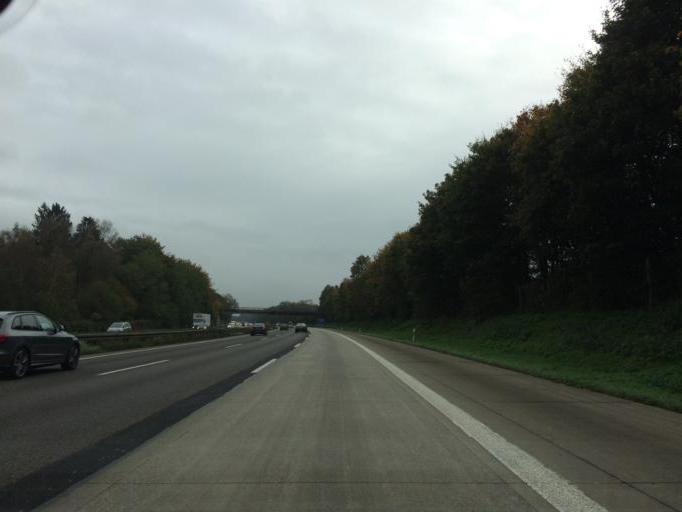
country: DE
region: North Rhine-Westphalia
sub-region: Regierungsbezirk Dusseldorf
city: Hochfeld
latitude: 51.3748
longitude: 6.8225
